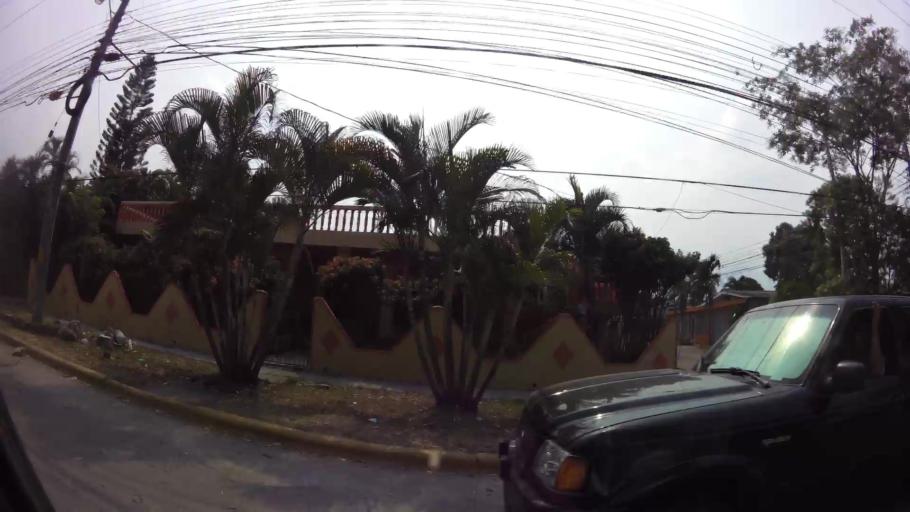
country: HN
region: Cortes
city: San Pedro Sula
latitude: 15.4886
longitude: -88.0328
